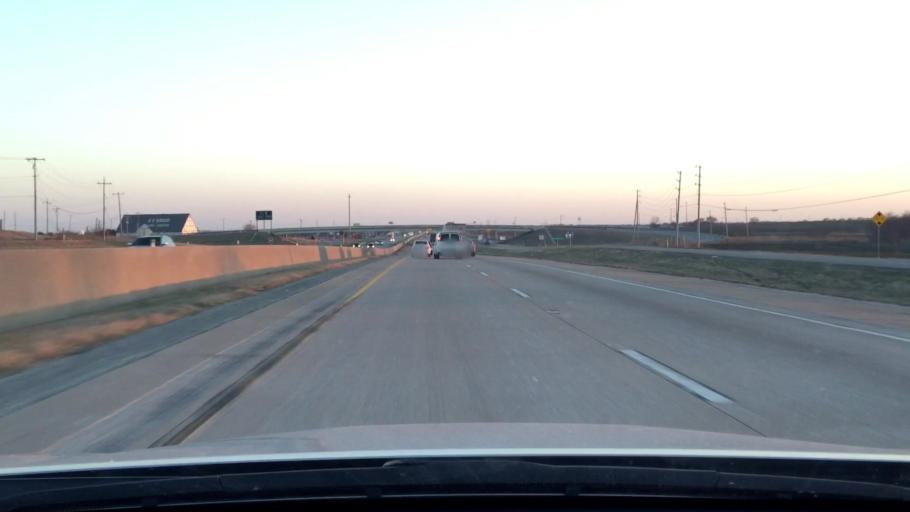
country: US
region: Texas
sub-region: Denton County
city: Sanger
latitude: 33.3962
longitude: -97.1768
